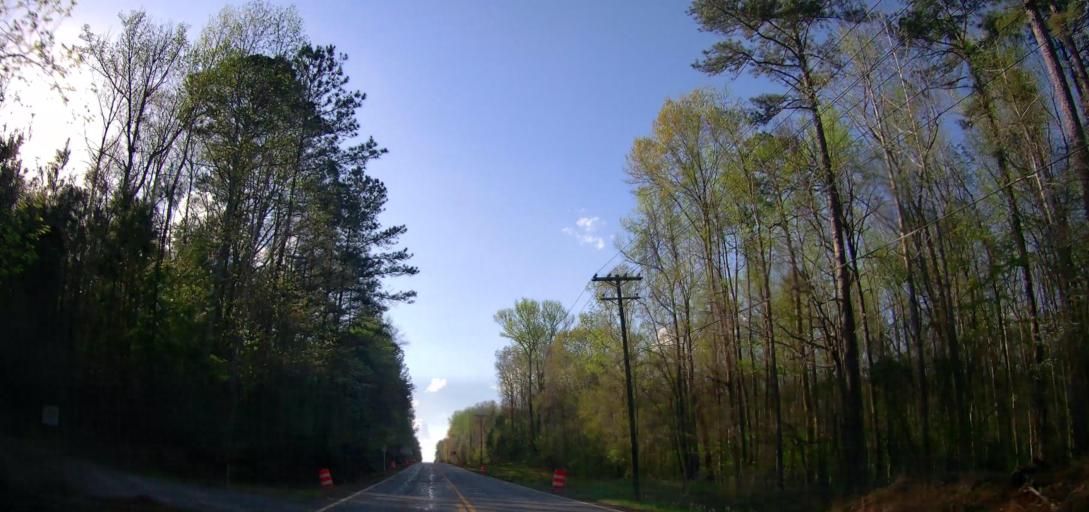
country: US
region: Georgia
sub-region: Putnam County
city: Eatonton
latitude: 33.1656
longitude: -83.3794
